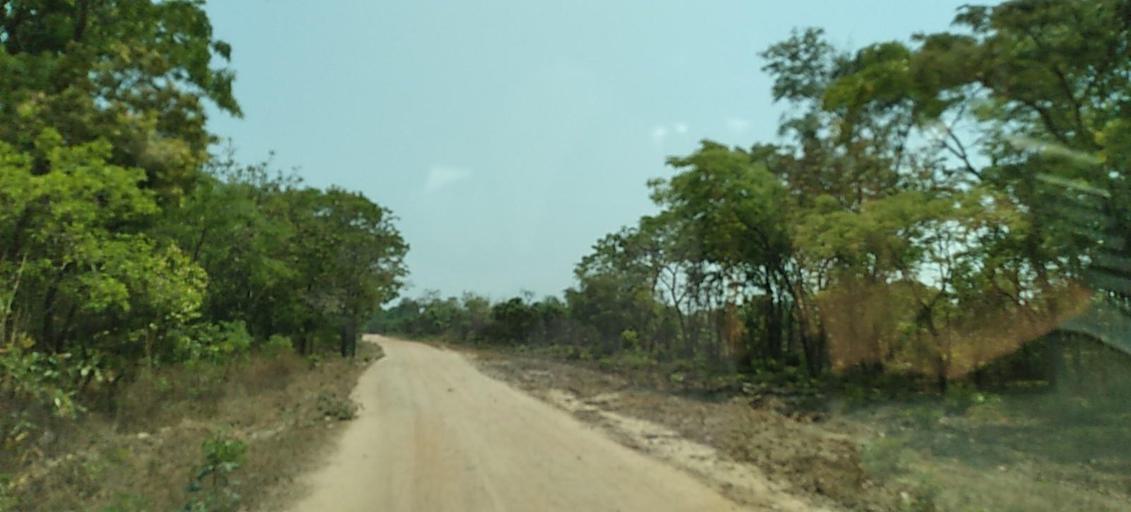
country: ZM
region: Copperbelt
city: Kalulushi
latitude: -12.9461
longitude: 28.1526
